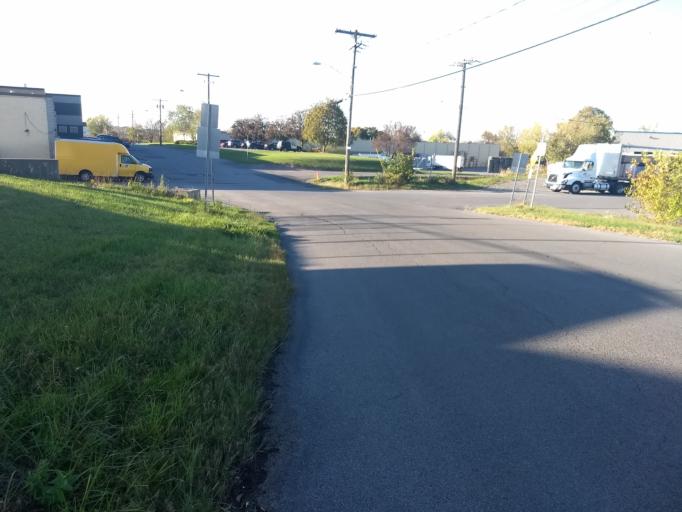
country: US
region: New York
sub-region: Onondaga County
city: Mattydale
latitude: 43.0852
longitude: -76.1434
